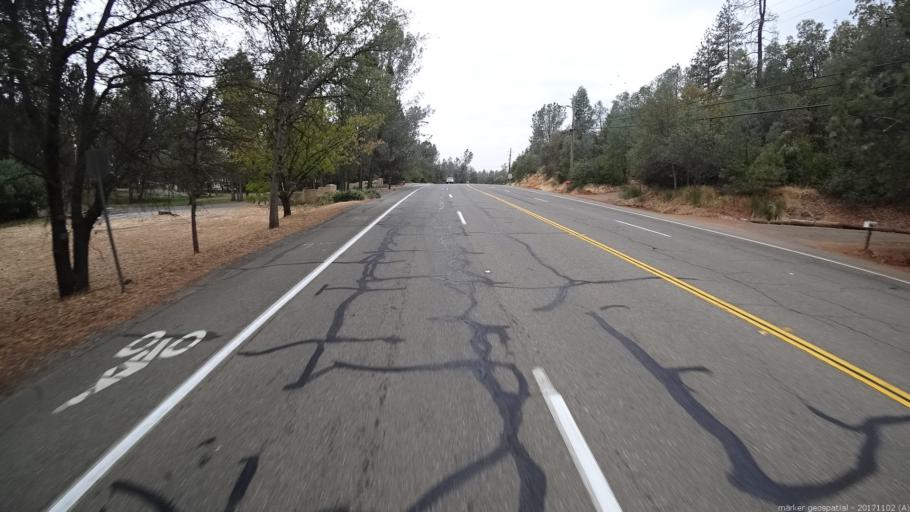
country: US
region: California
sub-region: Shasta County
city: Central Valley (historical)
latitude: 40.6388
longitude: -122.4018
